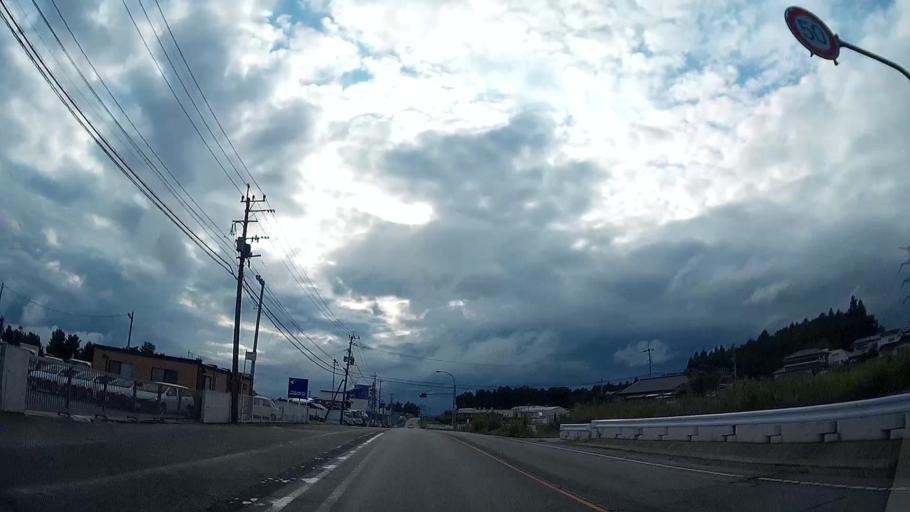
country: JP
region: Kumamoto
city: Ozu
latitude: 32.8772
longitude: 130.9210
